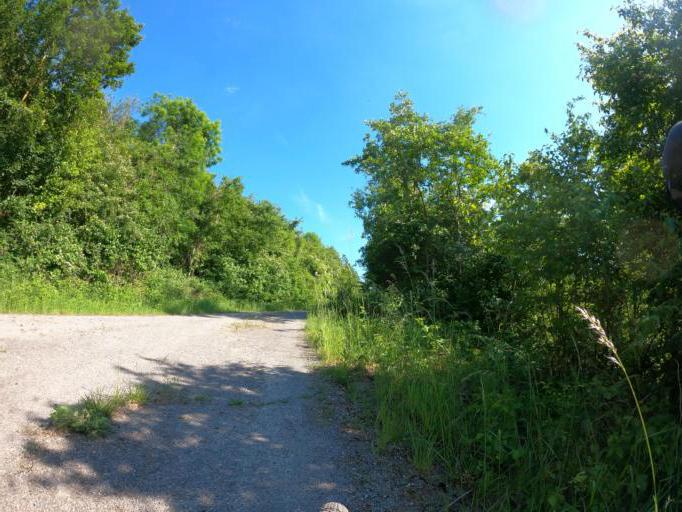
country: DE
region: Baden-Wuerttemberg
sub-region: Regierungsbezirk Stuttgart
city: Leonberg
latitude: 48.7604
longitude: 9.0340
